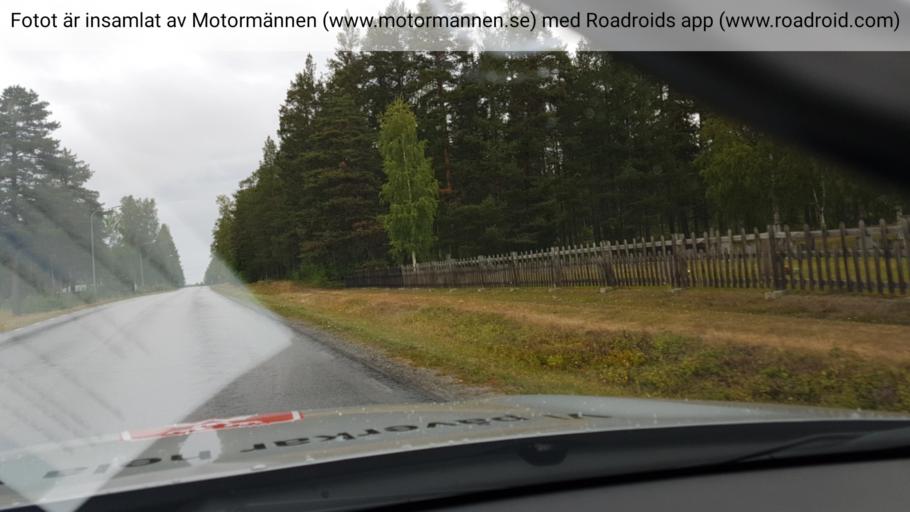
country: SE
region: Norrbotten
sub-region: Alvsbyns Kommun
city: AElvsbyn
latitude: 66.0923
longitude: 20.9459
